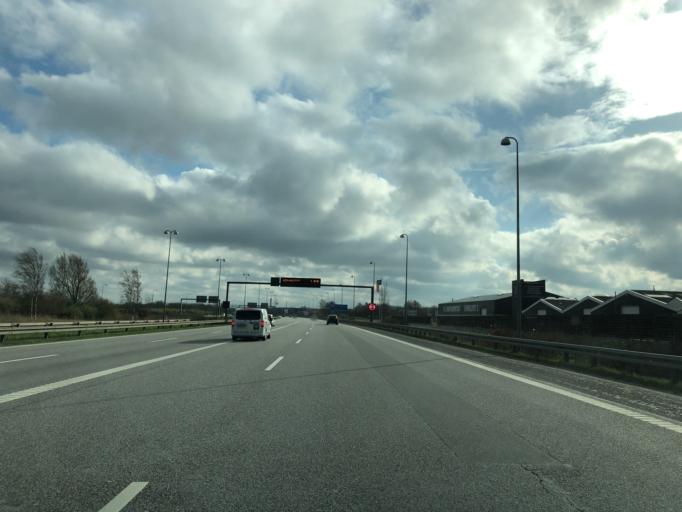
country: DK
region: North Denmark
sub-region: Alborg Kommune
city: Vestbjerg
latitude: 57.0816
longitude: 9.9632
